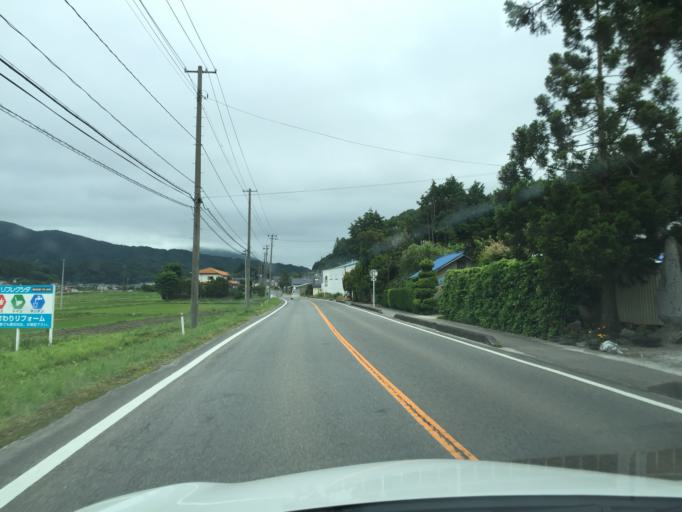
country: JP
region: Fukushima
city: Funehikimachi-funehiki
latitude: 37.3369
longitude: 140.6538
